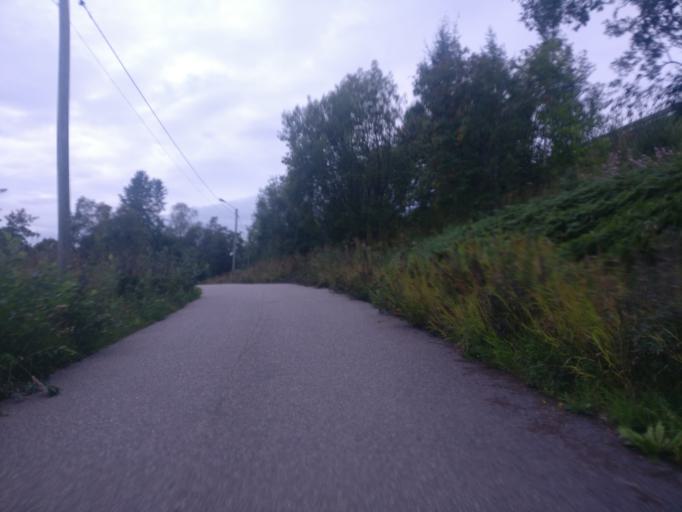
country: SE
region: Vaesternorrland
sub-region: Sundsvalls Kommun
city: Stockvik
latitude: 62.3628
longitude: 17.3700
